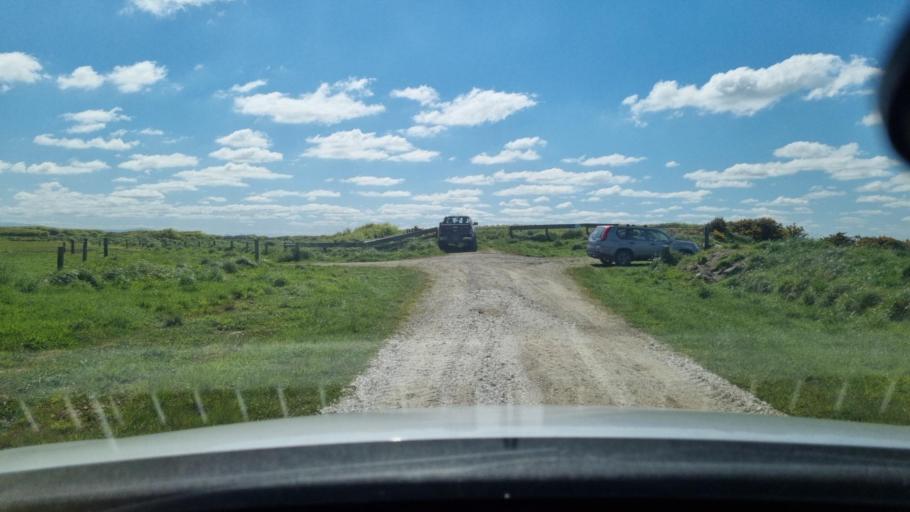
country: NZ
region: Southland
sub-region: Invercargill City
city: Invercargill
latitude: -46.3846
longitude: 168.2570
